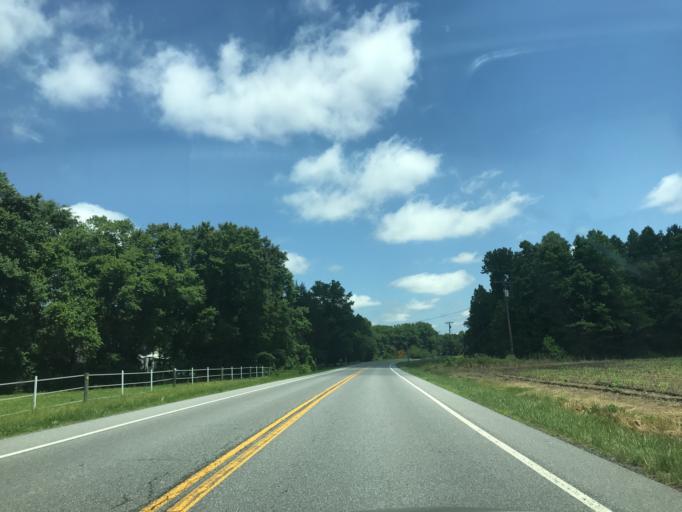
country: US
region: Maryland
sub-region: Caroline County
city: Federalsburg
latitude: 38.7400
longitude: -75.7229
